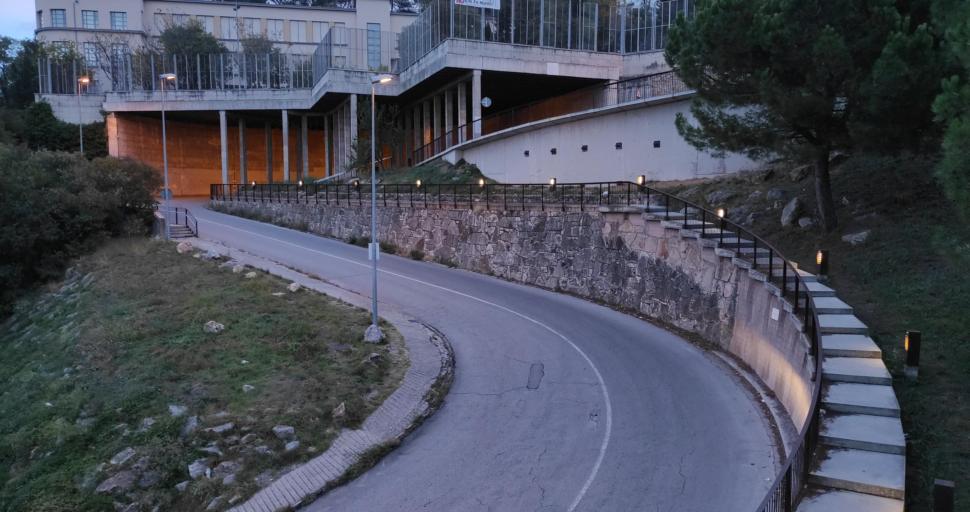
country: ES
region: Catalonia
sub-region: Provincia de Girona
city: Girona
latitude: 41.9902
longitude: 2.8265
